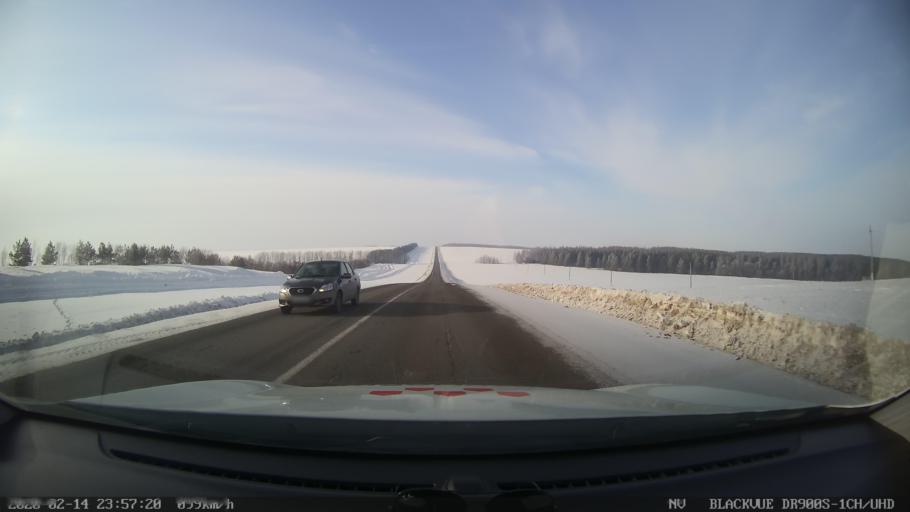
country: RU
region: Tatarstan
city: Kuybyshevskiy Zaton
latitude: 55.3331
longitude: 49.1120
